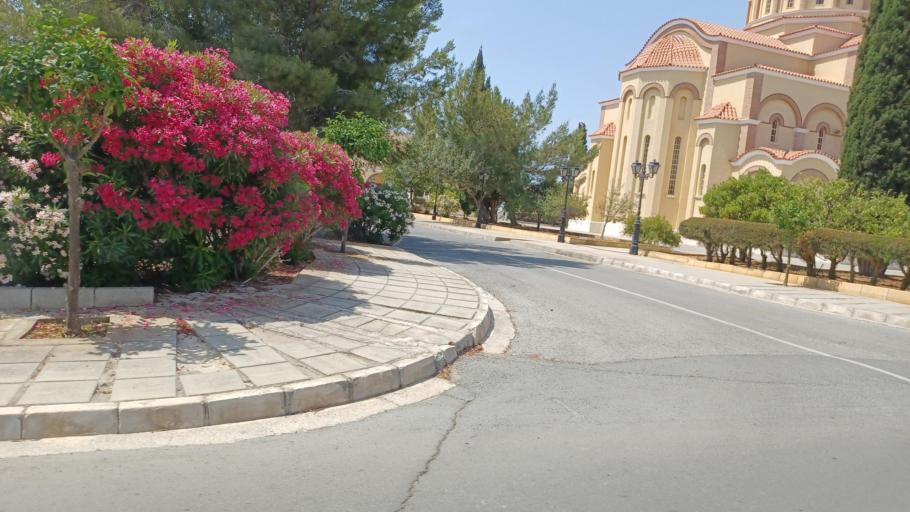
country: CY
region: Ammochostos
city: Paralimni
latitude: 35.0500
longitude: 33.9829
